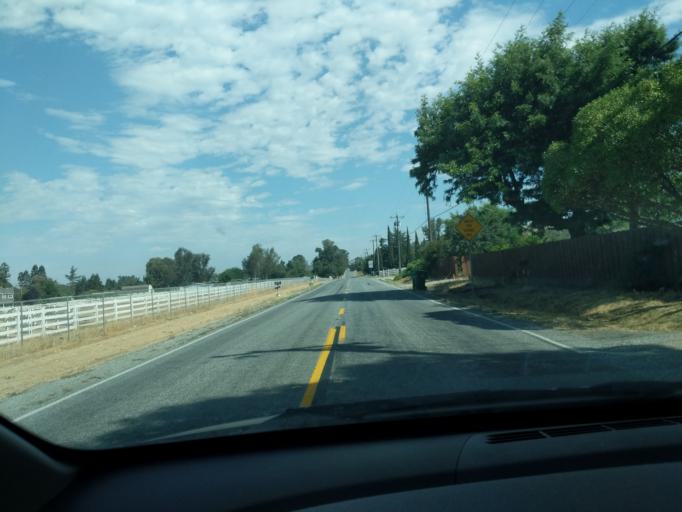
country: US
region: California
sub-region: Santa Clara County
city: Gilroy
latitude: 37.0637
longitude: -121.5540
